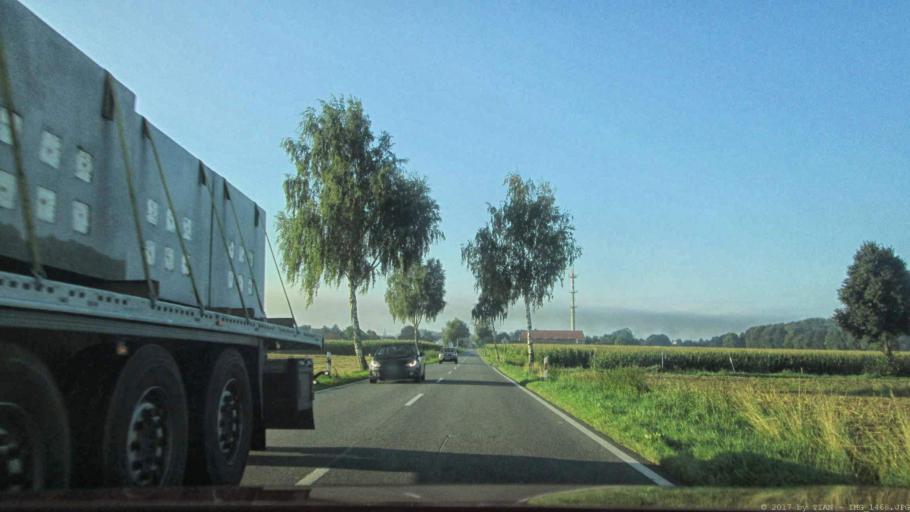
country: DE
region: Lower Saxony
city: Wittingen
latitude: 52.7396
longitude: 10.7355
